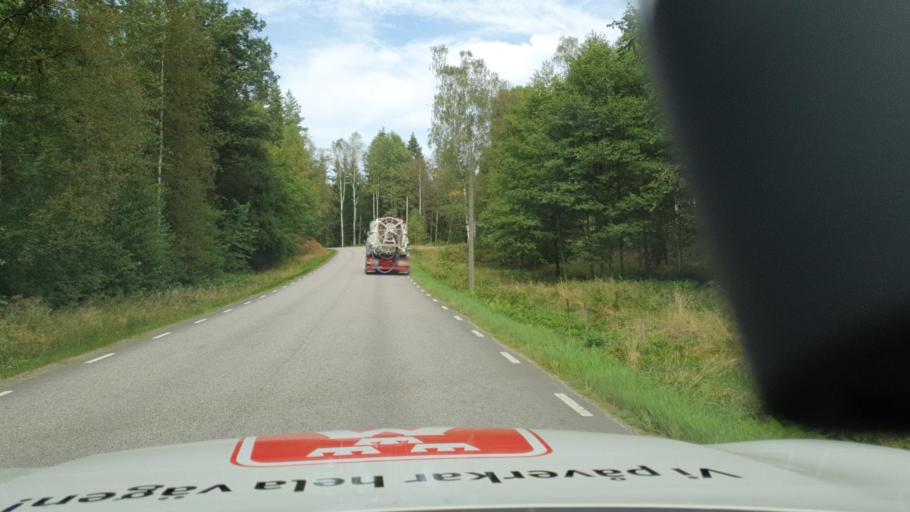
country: SE
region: Vaestra Goetaland
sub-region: Marks Kommun
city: Kinna
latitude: 57.4184
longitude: 12.6861
